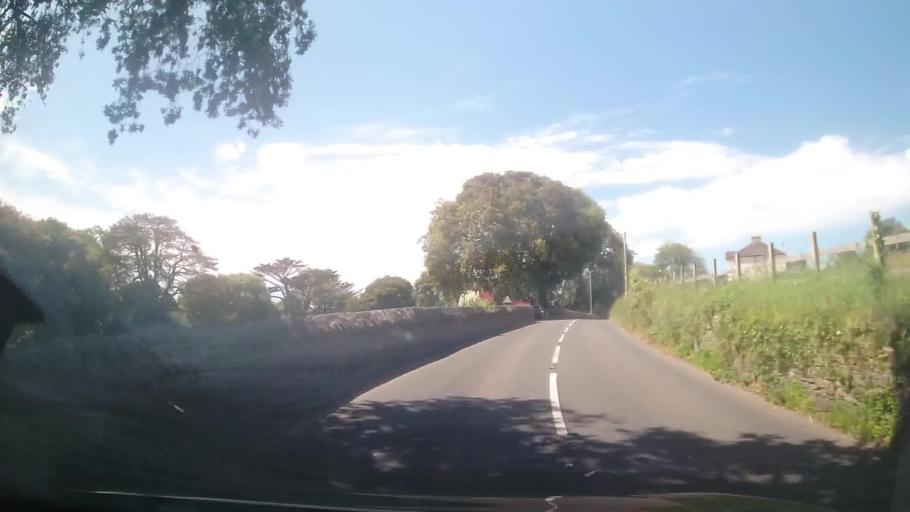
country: GB
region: England
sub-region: Devon
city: Kingsbridge
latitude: 50.2736
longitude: -3.7645
